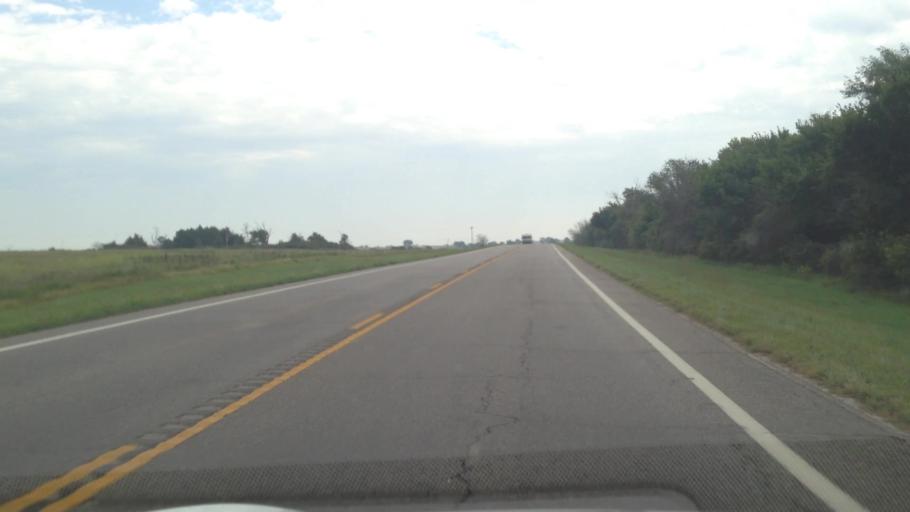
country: US
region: Kansas
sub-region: Bourbon County
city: Fort Scott
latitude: 37.8902
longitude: -95.0353
